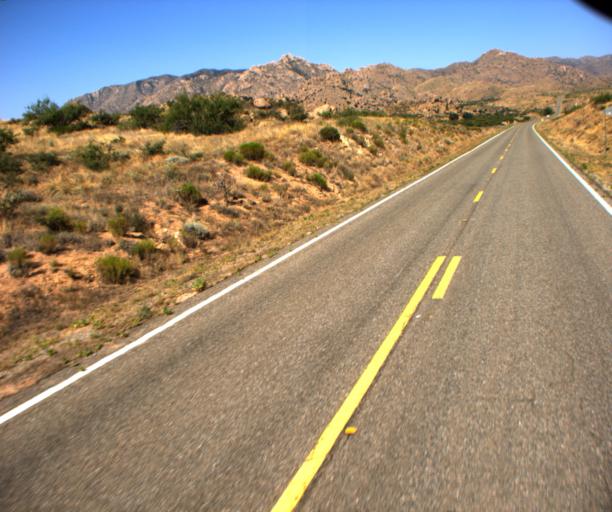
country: US
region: Arizona
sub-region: Graham County
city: Swift Trail Junction
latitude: 32.5601
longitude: -109.7478
